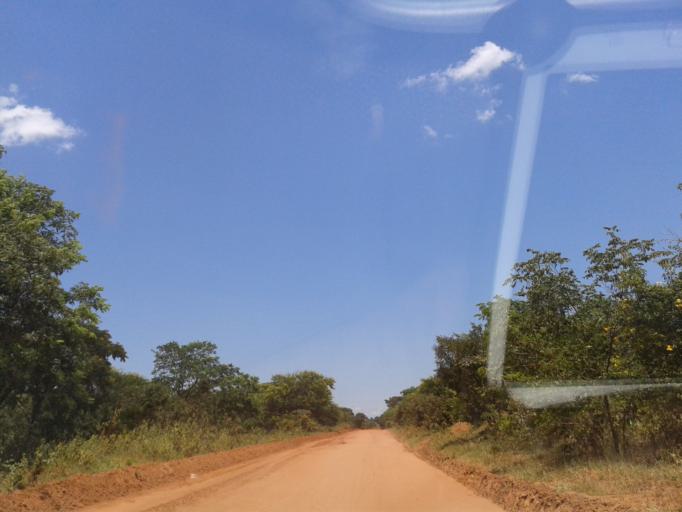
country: BR
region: Minas Gerais
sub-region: Santa Vitoria
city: Santa Vitoria
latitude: -19.2148
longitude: -50.3872
